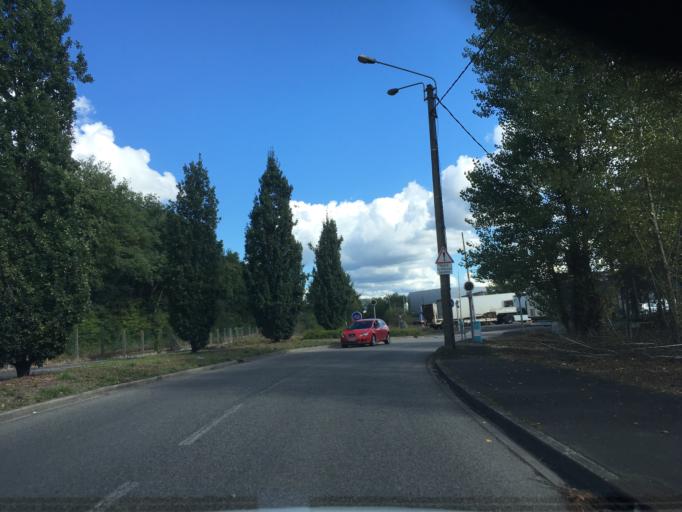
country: FR
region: Limousin
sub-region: Departement de la Correze
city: Saint-Pantaleon-de-Larche
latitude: 45.1538
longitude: 1.4867
